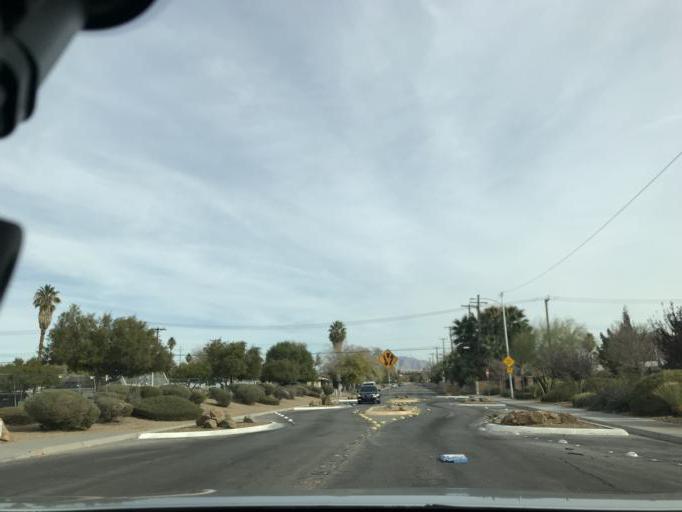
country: US
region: Nevada
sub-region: Clark County
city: Las Vegas
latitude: 36.1734
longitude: -115.1708
